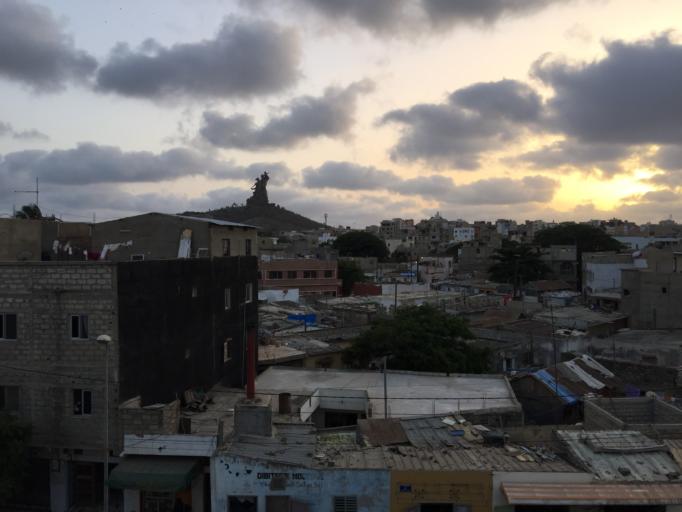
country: SN
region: Dakar
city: Mermoz Boabab
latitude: 14.7250
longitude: -17.4880
